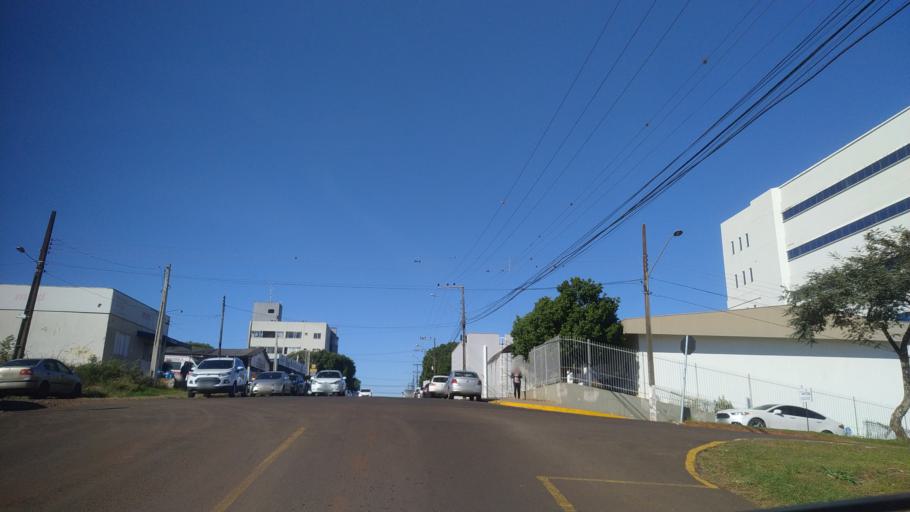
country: BR
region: Santa Catarina
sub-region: Chapeco
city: Chapeco
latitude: -27.1069
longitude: -52.5978
